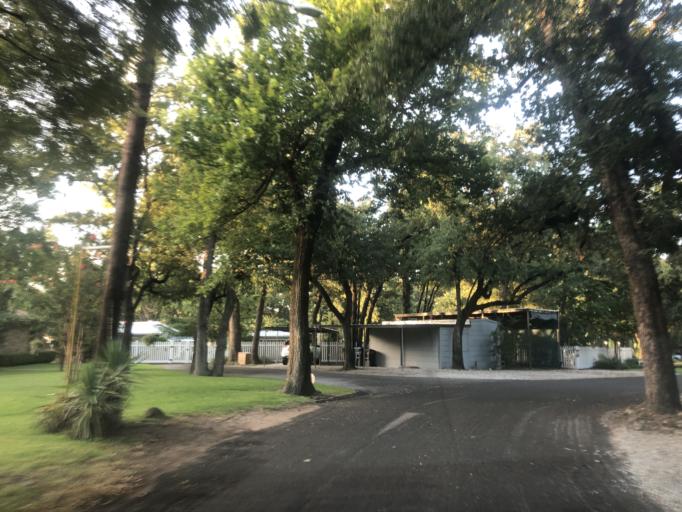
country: US
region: Texas
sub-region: Tarrant County
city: Lakeside
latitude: 32.7984
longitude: -97.4897
